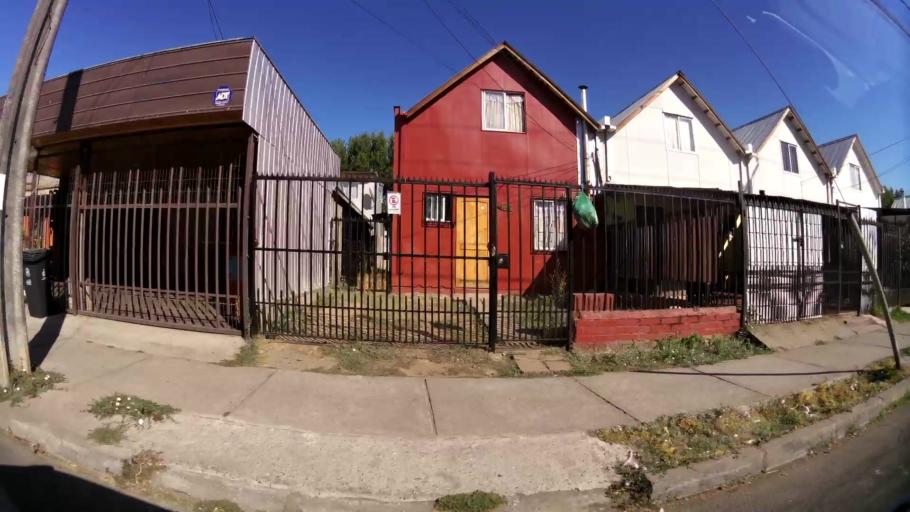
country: CL
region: Maule
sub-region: Provincia de Curico
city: Curico
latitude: -34.9913
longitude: -71.2591
